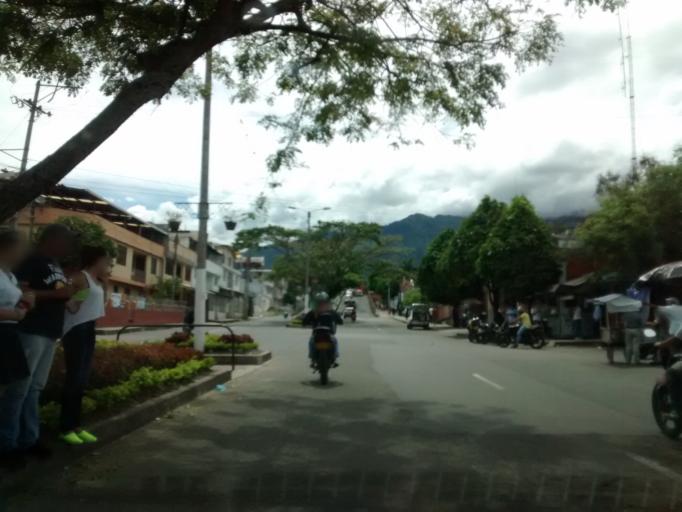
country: CO
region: Tolima
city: Ibague
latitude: 4.4341
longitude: -75.2015
